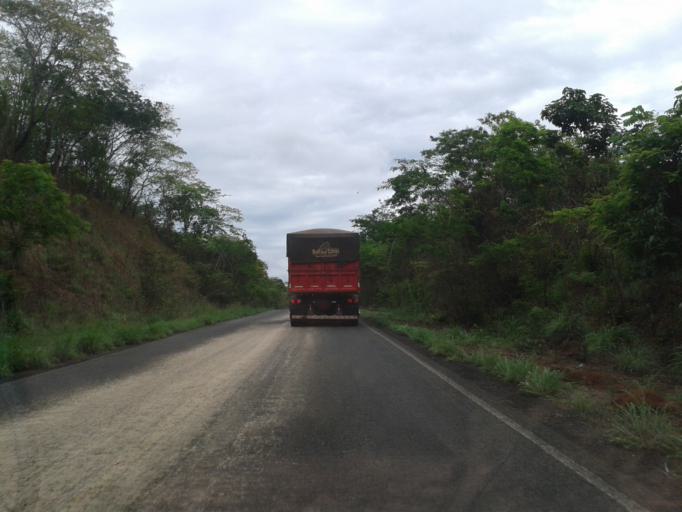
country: BR
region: Goias
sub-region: Caldas Novas
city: Caldas Novas
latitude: -18.0636
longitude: -48.6794
